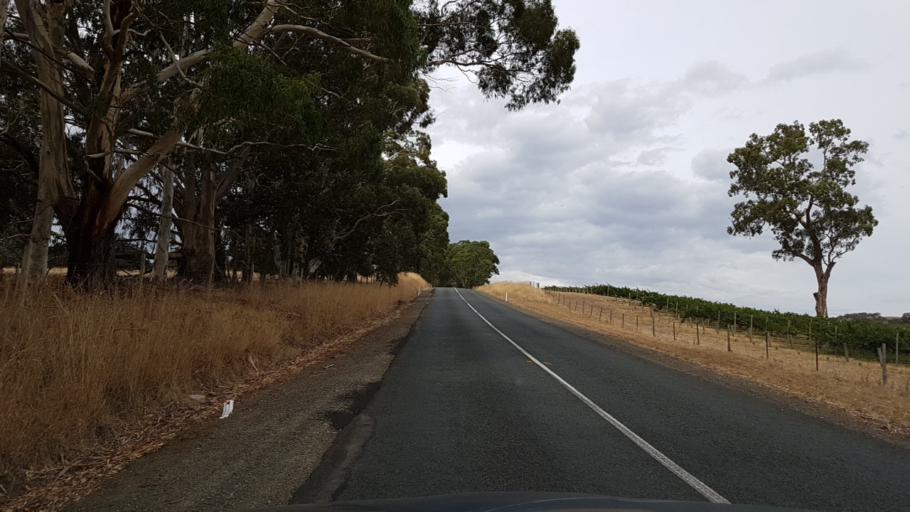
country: AU
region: South Australia
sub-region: Adelaide Hills
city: Gumeracha
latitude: -34.7821
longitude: 138.9147
